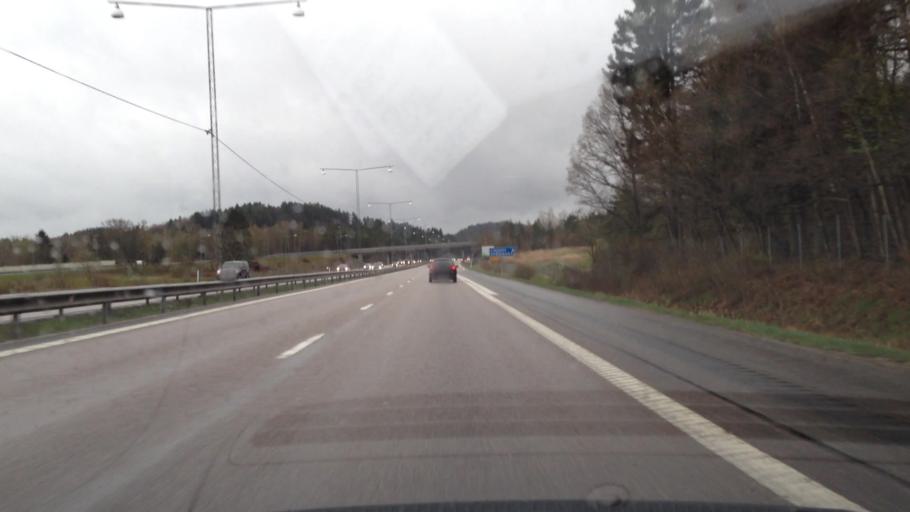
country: SE
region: Vaestra Goetaland
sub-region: Molndal
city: Lindome
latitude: 57.5757
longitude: 12.0599
